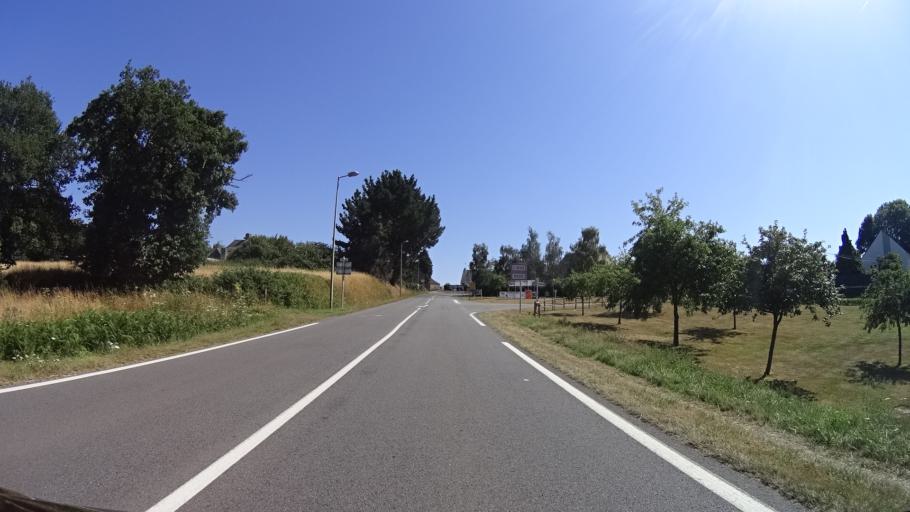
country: FR
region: Brittany
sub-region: Departement du Morbihan
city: Rieux
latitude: 47.5998
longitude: -2.1039
